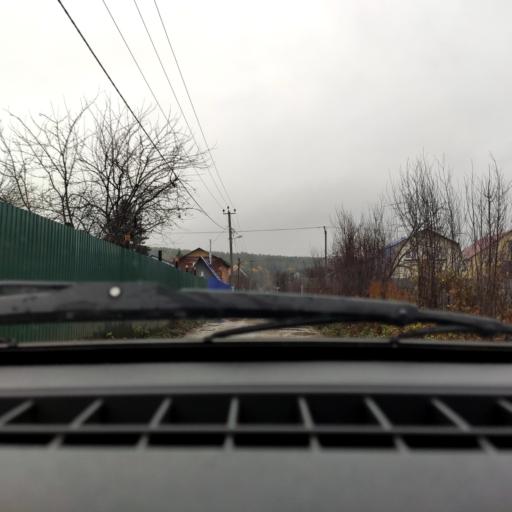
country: RU
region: Bashkortostan
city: Ufa
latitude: 54.8103
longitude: 56.1540
